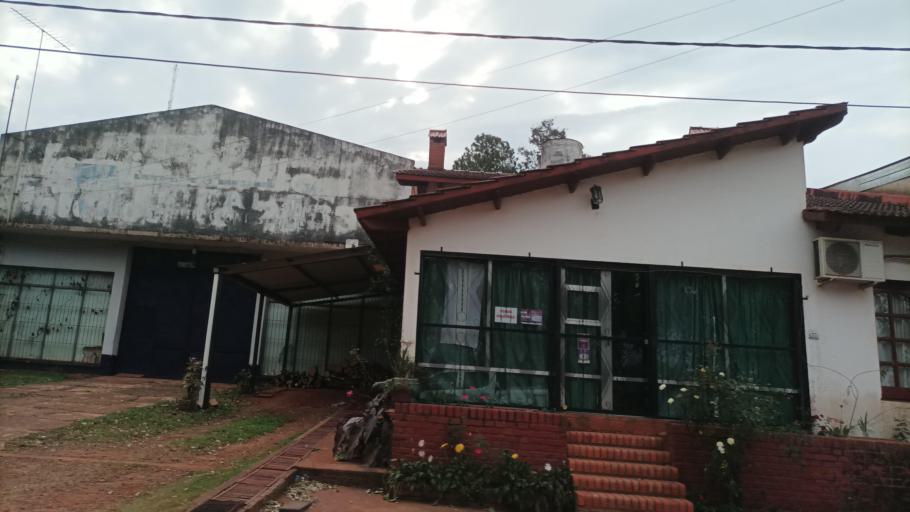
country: AR
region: Misiones
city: Aristobulo del Valle
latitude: -27.0951
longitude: -54.8921
